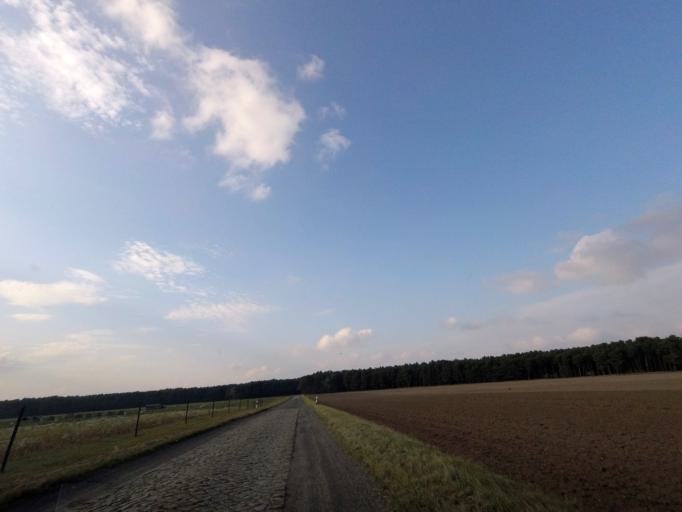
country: DE
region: Brandenburg
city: Linthe
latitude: 52.1554
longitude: 12.7161
